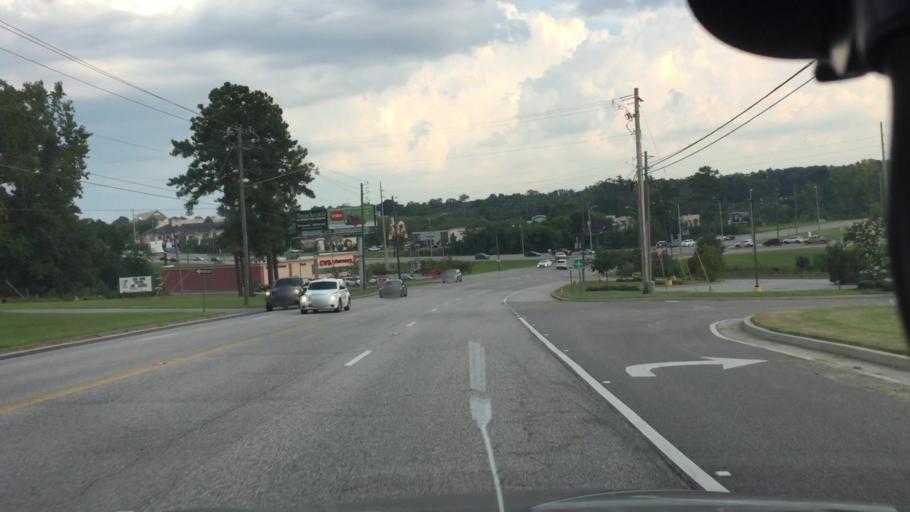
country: US
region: Alabama
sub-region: Coffee County
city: Enterprise
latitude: 31.3309
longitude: -85.8383
